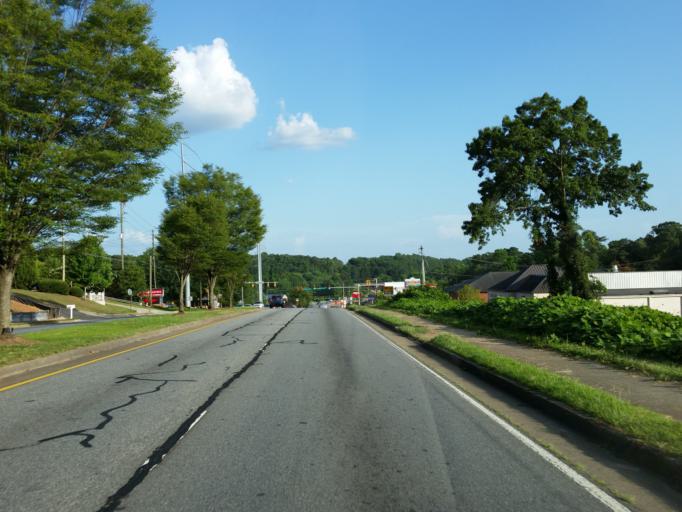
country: US
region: Georgia
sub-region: Cherokee County
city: Woodstock
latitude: 34.0596
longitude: -84.5586
